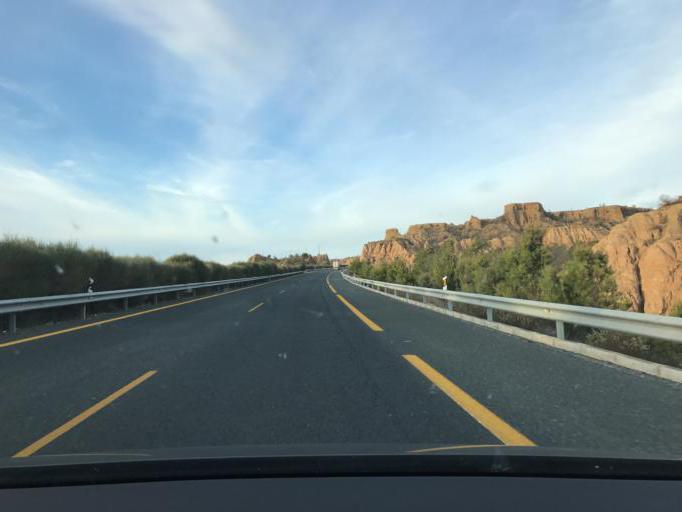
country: ES
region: Andalusia
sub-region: Provincia de Granada
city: Guadix
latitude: 37.3080
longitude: -3.1121
